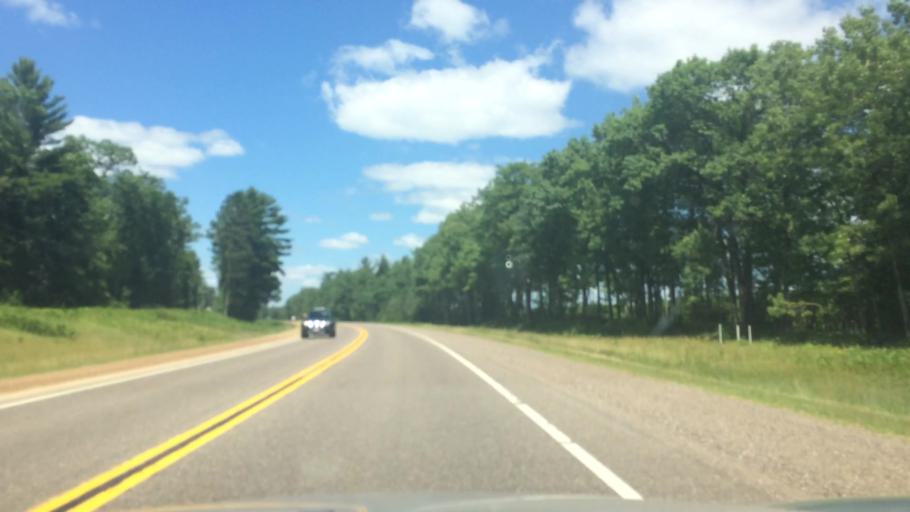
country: US
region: Wisconsin
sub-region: Vilas County
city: Lac du Flambeau
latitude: 45.9420
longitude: -89.6967
